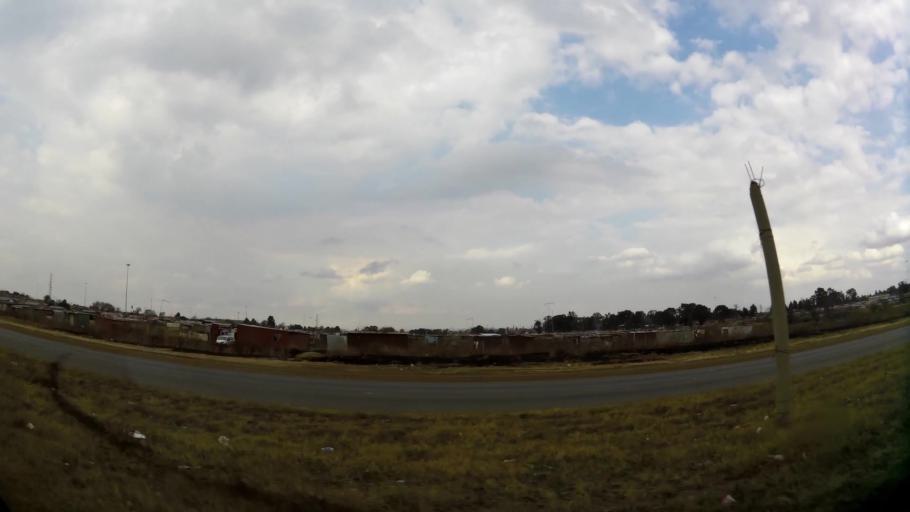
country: ZA
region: Gauteng
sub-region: Sedibeng District Municipality
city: Vanderbijlpark
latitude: -26.6651
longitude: 27.8409
